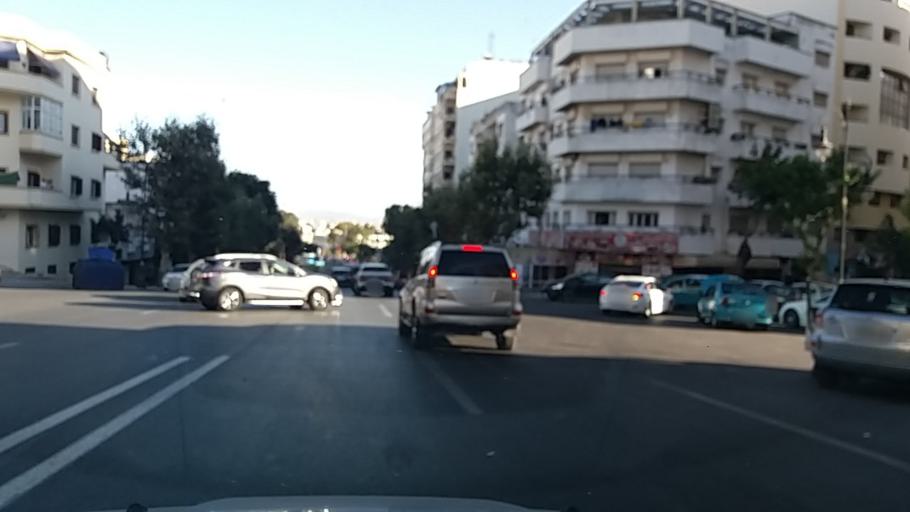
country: MA
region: Tanger-Tetouan
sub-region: Tanger-Assilah
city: Tangier
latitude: 35.7792
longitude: -5.8200
